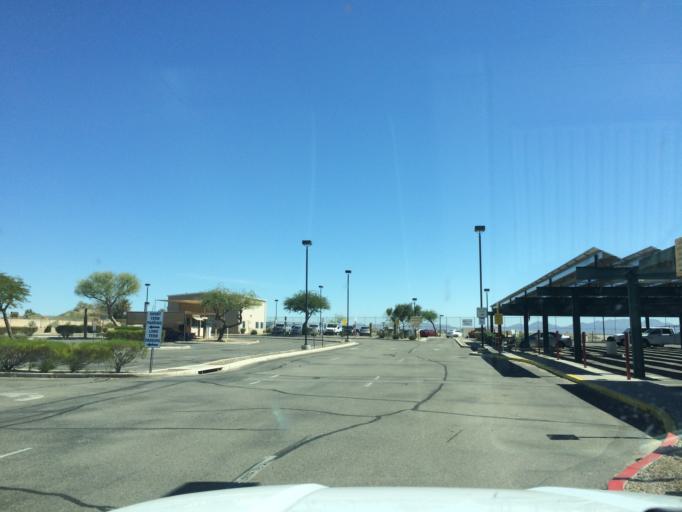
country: US
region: Arizona
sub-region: Yuma County
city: Yuma
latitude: 32.6685
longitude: -114.5982
